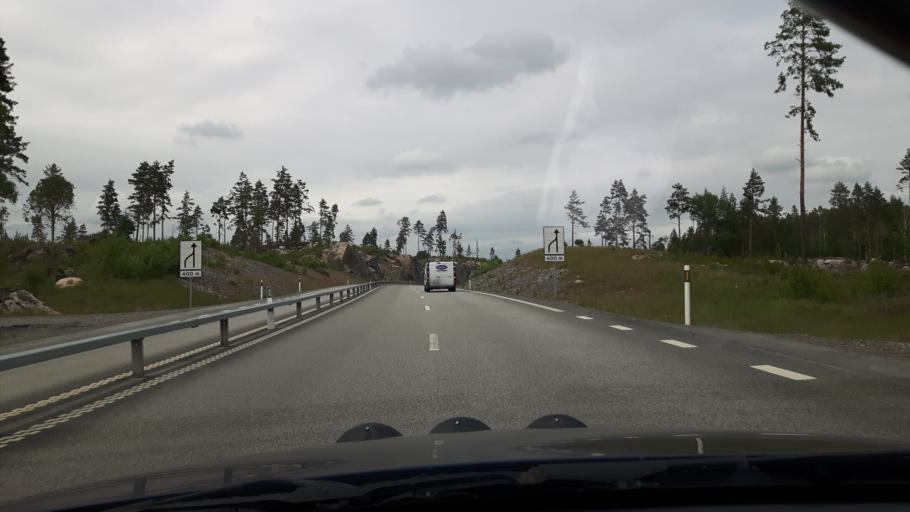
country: SE
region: Soedermanland
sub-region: Flens Kommun
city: Malmkoping
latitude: 59.1227
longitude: 16.6667
